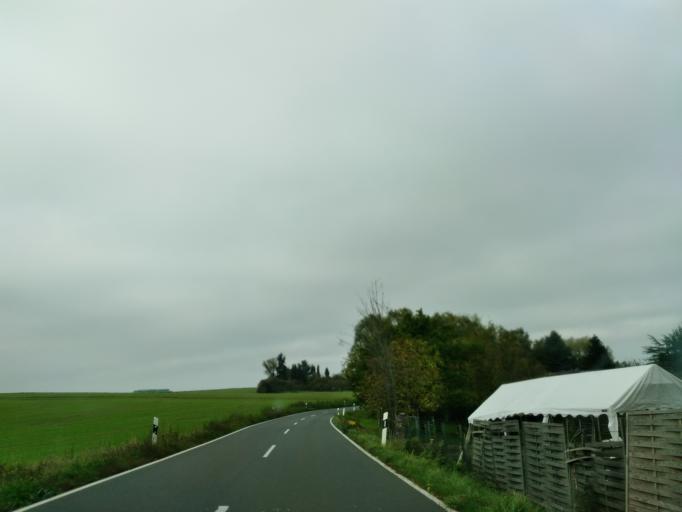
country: DE
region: North Rhine-Westphalia
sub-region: Regierungsbezirk Koln
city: Konigswinter
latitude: 50.7134
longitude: 7.2006
